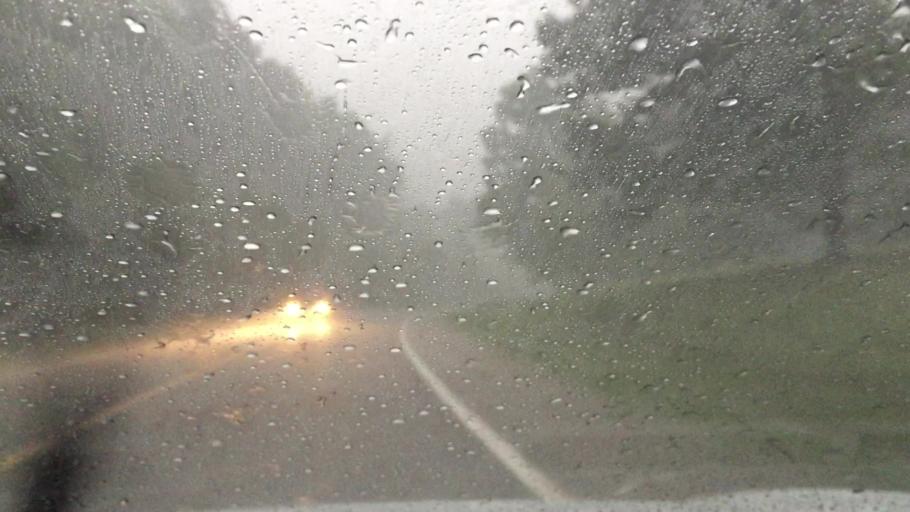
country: CA
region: Ontario
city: Markham
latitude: 43.8497
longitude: -79.2010
